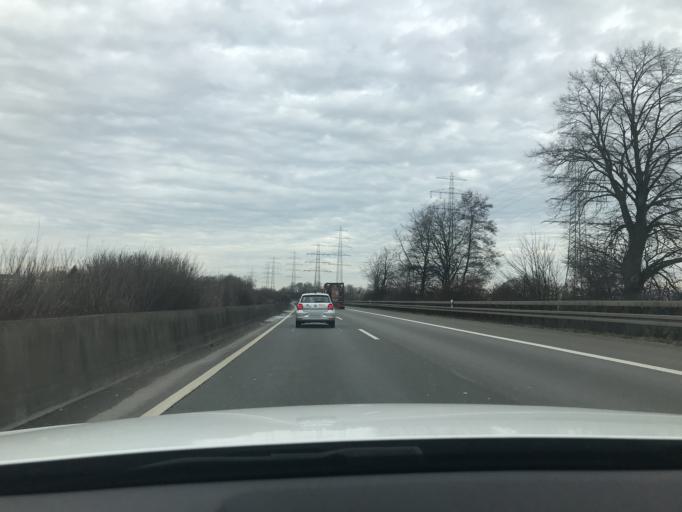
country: DE
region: North Rhine-Westphalia
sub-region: Regierungsbezirk Dusseldorf
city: Dormagen
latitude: 51.1299
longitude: 6.7915
